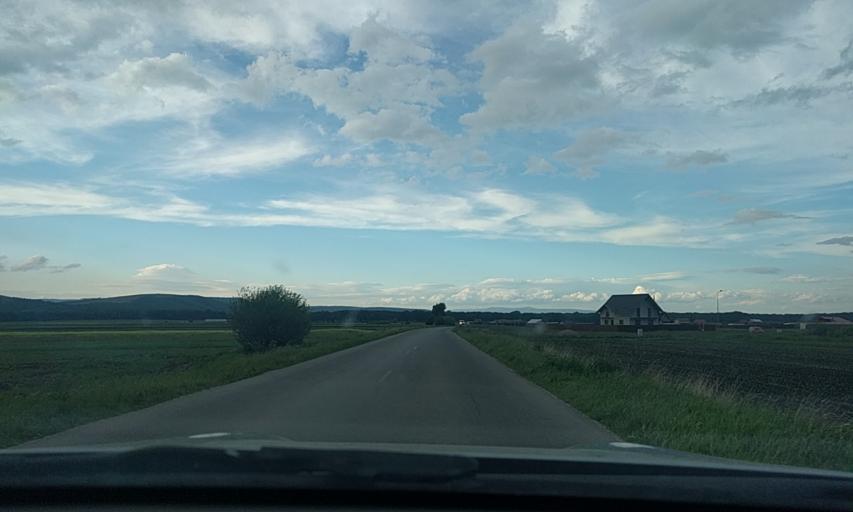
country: RO
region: Brasov
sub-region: Comuna Harman
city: Harman
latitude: 45.7330
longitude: 25.7013
